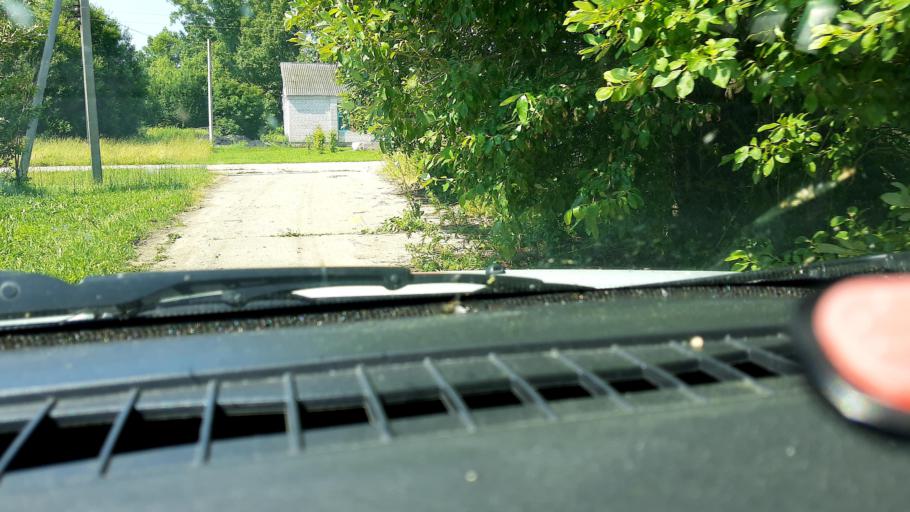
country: RU
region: Nizjnij Novgorod
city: Sharanga
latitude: 57.0411
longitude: 46.7185
